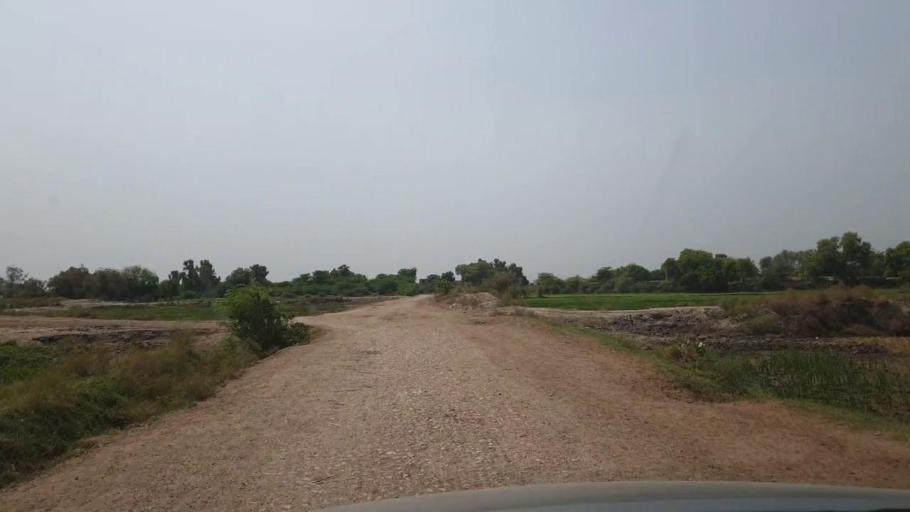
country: PK
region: Sindh
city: Madeji
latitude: 27.7986
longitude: 68.5401
